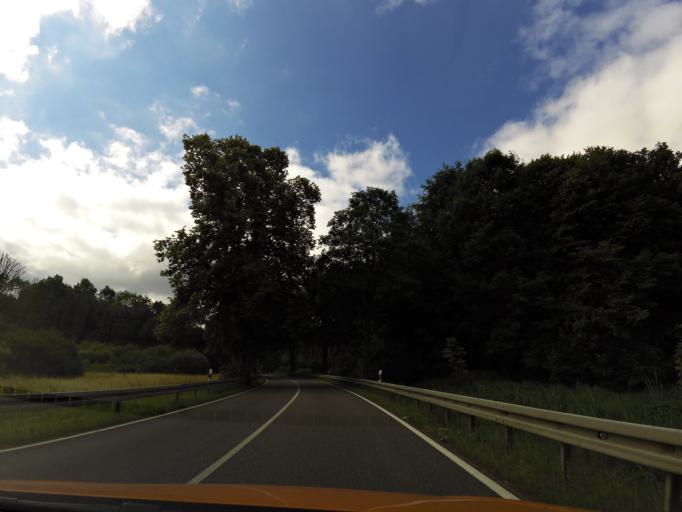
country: DE
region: Mecklenburg-Vorpommern
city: Krakow am See
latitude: 53.7155
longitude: 12.2763
